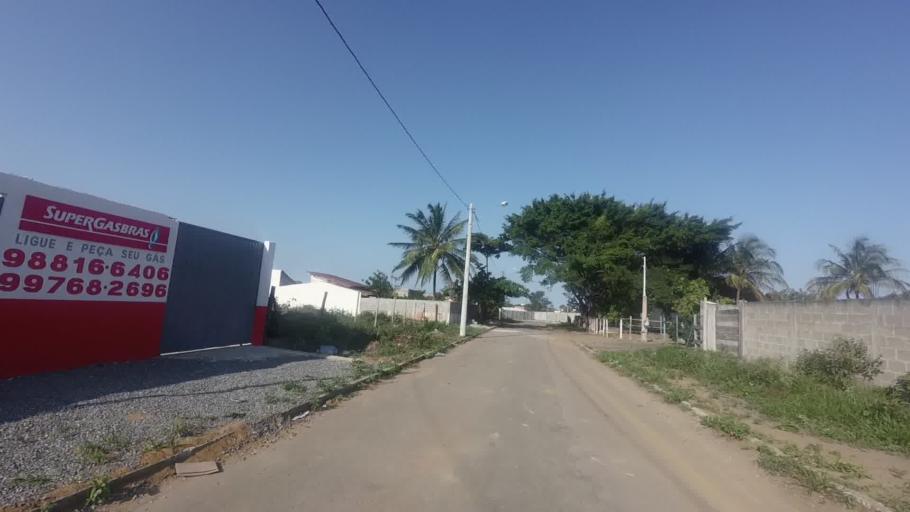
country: BR
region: Espirito Santo
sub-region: Guarapari
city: Guarapari
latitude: -20.7256
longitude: -40.5402
